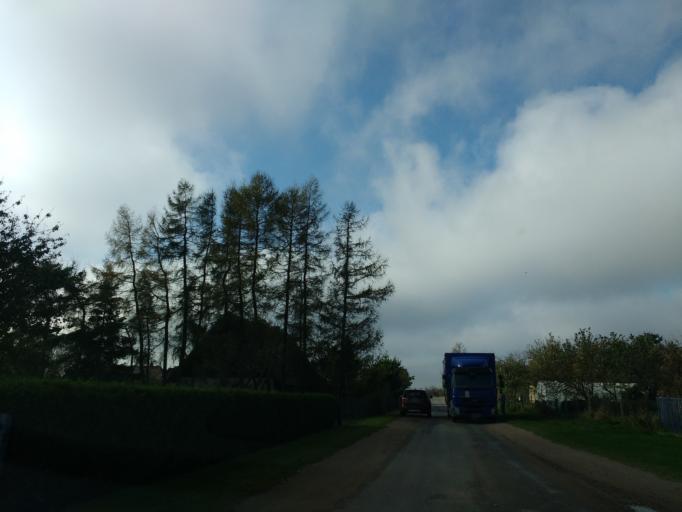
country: DE
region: Mecklenburg-Vorpommern
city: Kalkhorst
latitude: 53.9361
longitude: 11.0342
